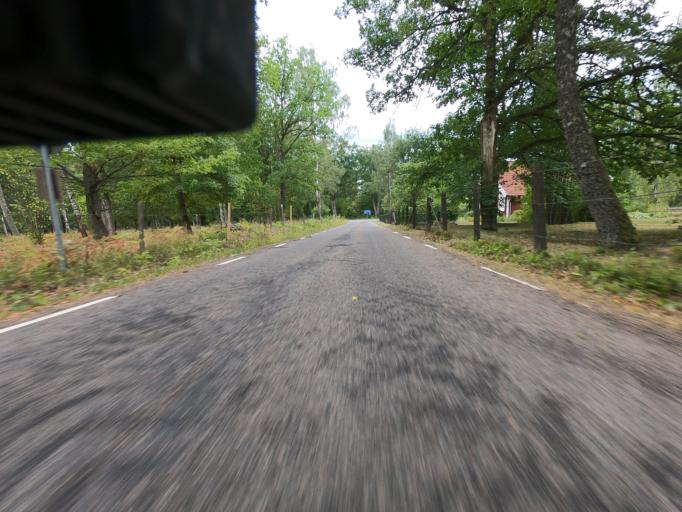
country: SE
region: Kronoberg
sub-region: Vaxjo Kommun
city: Rottne
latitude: 57.0838
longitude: 14.9463
